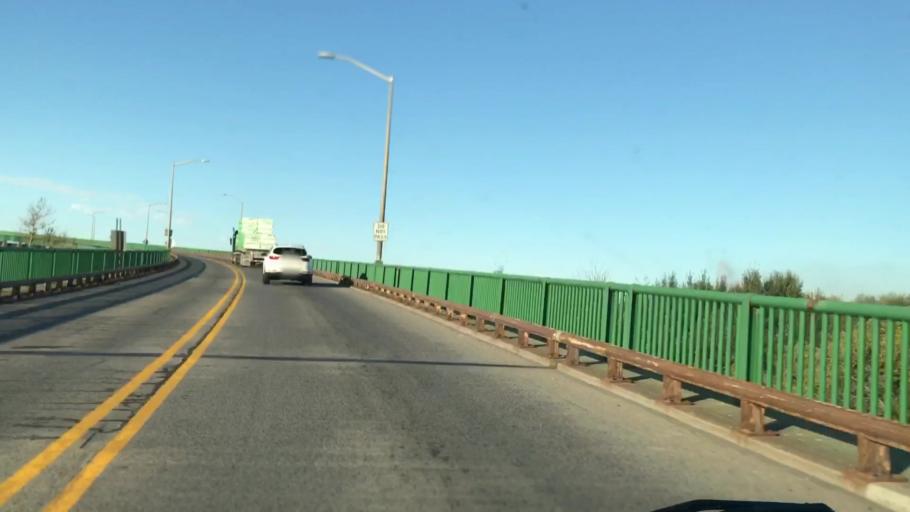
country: CA
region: Ontario
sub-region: Algoma
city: Sault Ste. Marie
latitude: 46.5187
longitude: -84.3540
